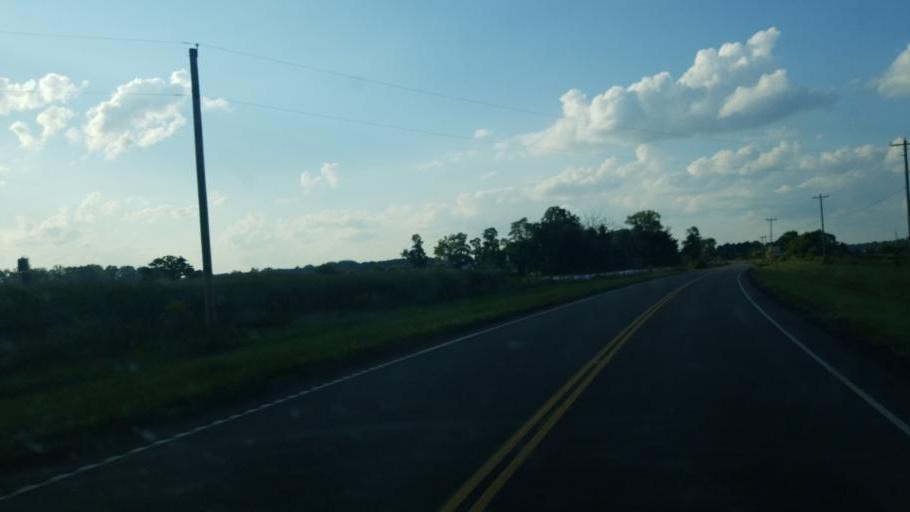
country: US
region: Ohio
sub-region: Knox County
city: Mount Vernon
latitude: 40.4262
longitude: -82.5087
